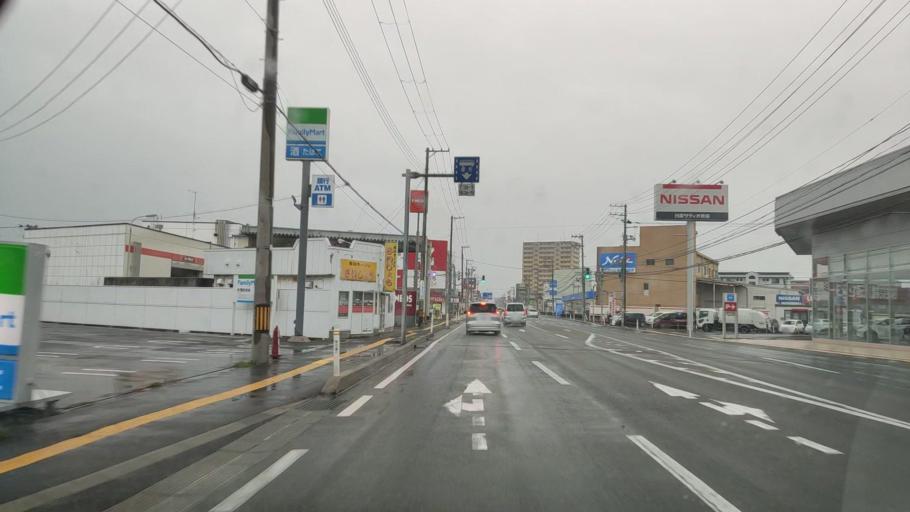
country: JP
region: Akita
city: Akita Shi
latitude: 39.7395
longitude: 140.0956
